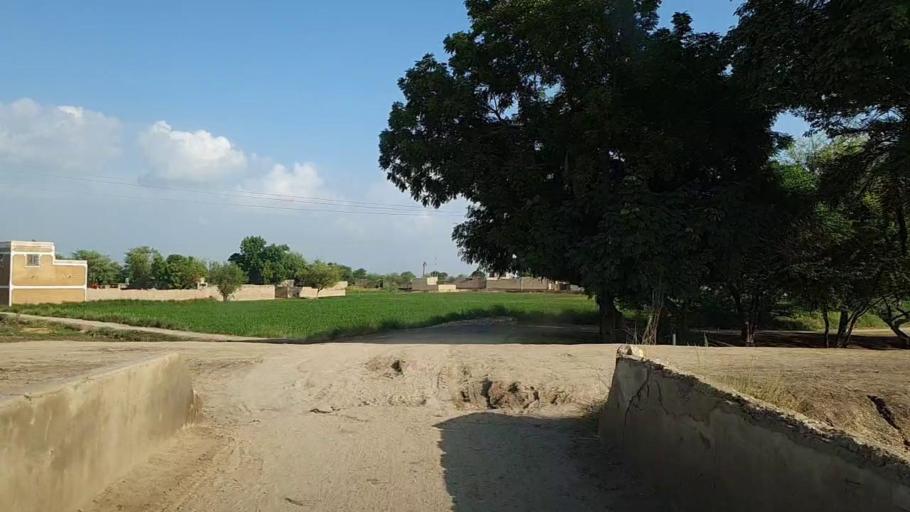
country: PK
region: Sindh
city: Hingorja
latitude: 27.0939
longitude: 68.3648
